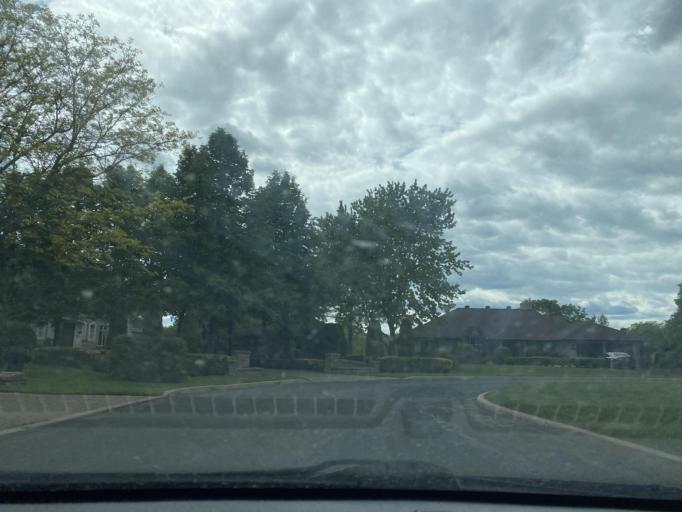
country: CA
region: Quebec
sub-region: Monteregie
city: Carignan
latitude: 45.4664
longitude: -73.2975
